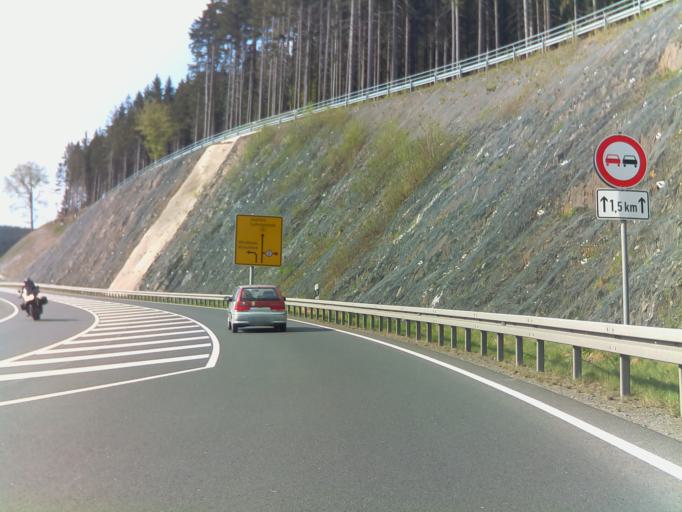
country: DE
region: Bavaria
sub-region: Upper Franconia
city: Teuschnitz
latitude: 50.4133
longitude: 11.3563
